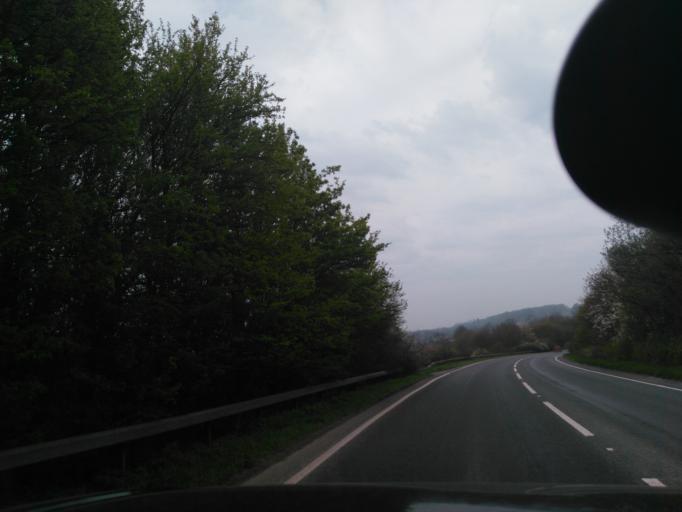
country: GB
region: England
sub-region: Somerset
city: Frome
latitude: 51.2072
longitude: -2.3199
